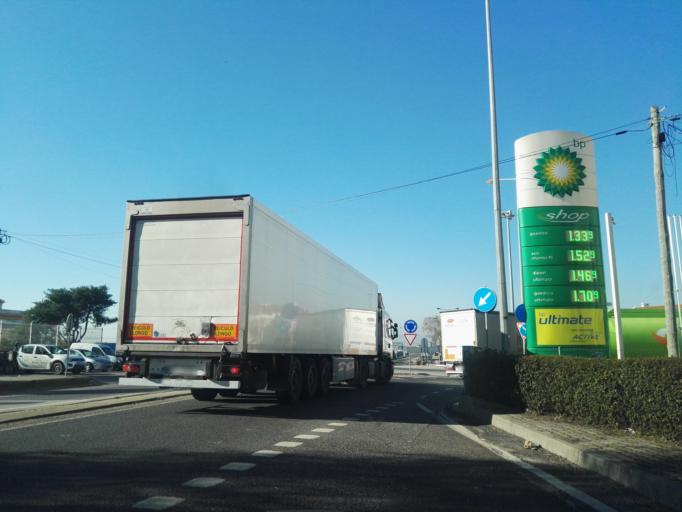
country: PT
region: Santarem
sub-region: Benavente
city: Samora Correia
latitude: 38.9237
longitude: -8.8880
